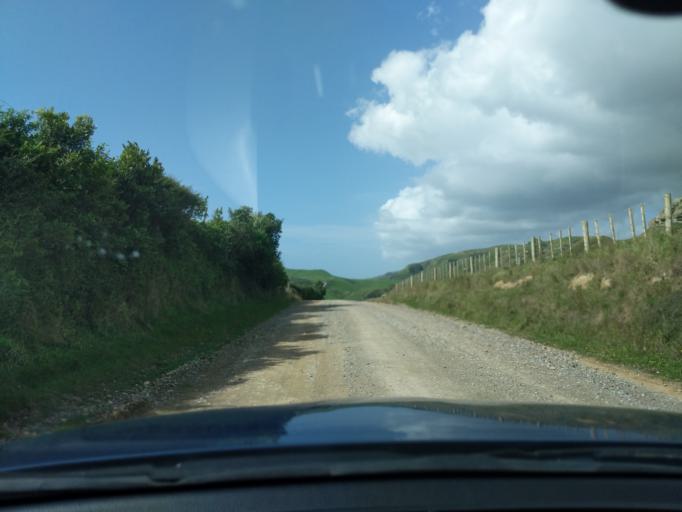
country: NZ
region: Tasman
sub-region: Tasman District
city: Takaka
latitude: -40.6484
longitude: 172.4272
